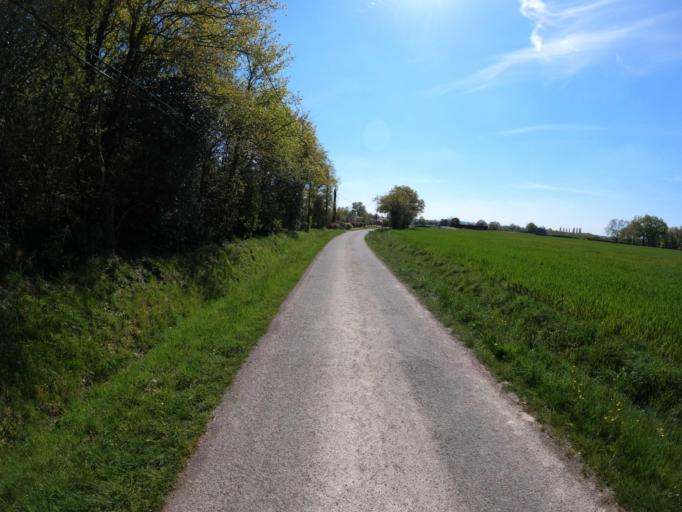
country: FR
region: Pays de la Loire
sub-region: Departement de la Loire-Atlantique
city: Remouille
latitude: 47.0667
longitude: -1.3602
